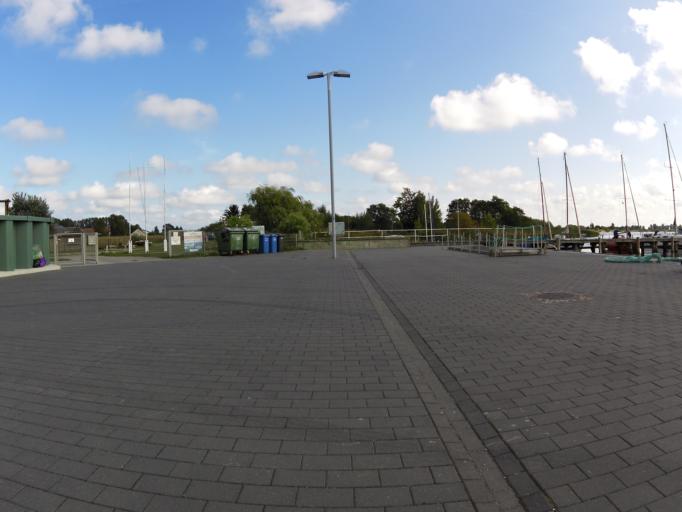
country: DE
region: Mecklenburg-Vorpommern
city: Kroslin
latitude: 54.1345
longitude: 13.7685
